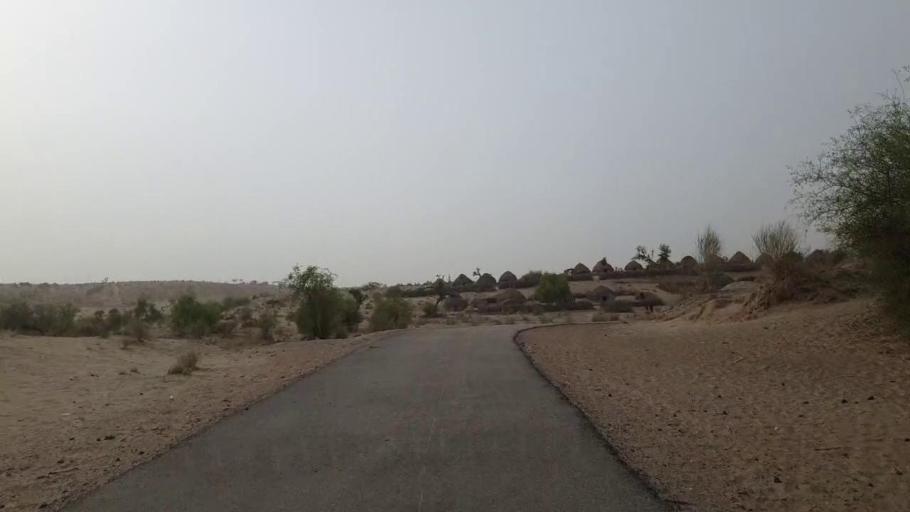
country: PK
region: Sindh
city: Islamkot
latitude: 24.5775
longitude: 70.3650
